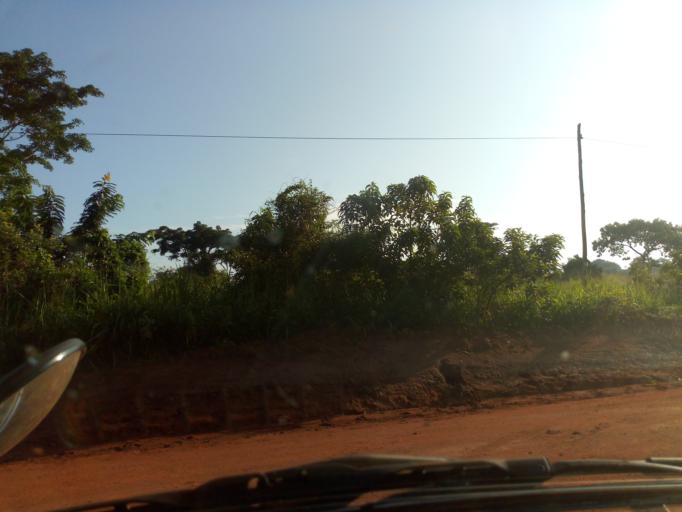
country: UG
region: Western Region
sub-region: Masindi District
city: Masindi
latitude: 1.7758
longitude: 31.8337
